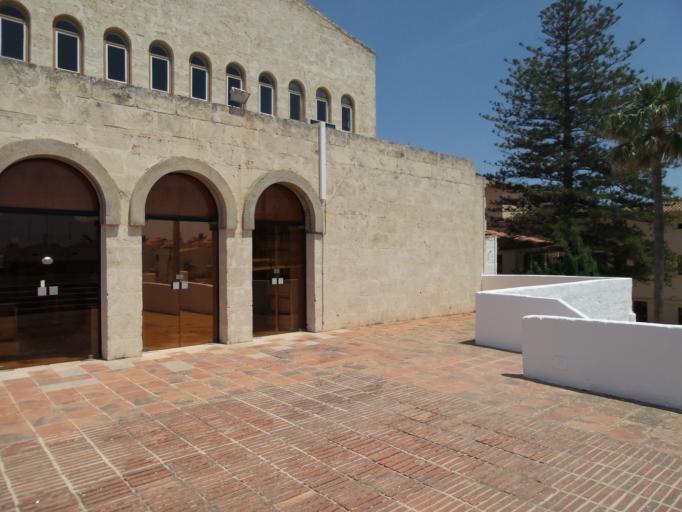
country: ES
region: Balearic Islands
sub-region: Illes Balears
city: Ciutadella
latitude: 40.0007
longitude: 3.8351
